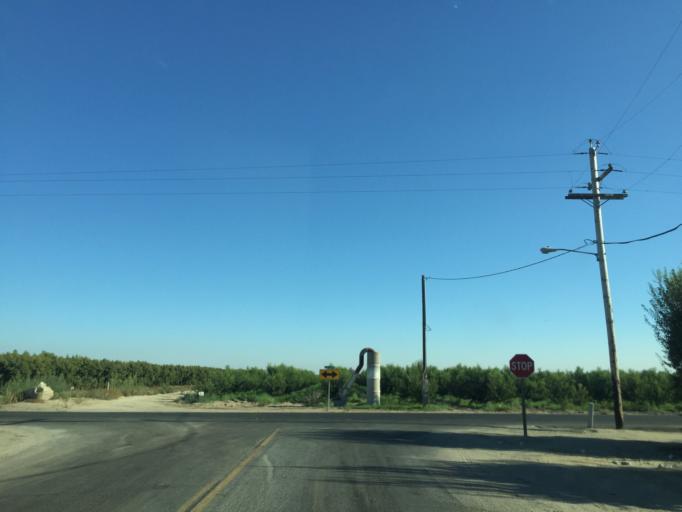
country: US
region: California
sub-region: Tulare County
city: London
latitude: 36.4592
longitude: -119.4389
